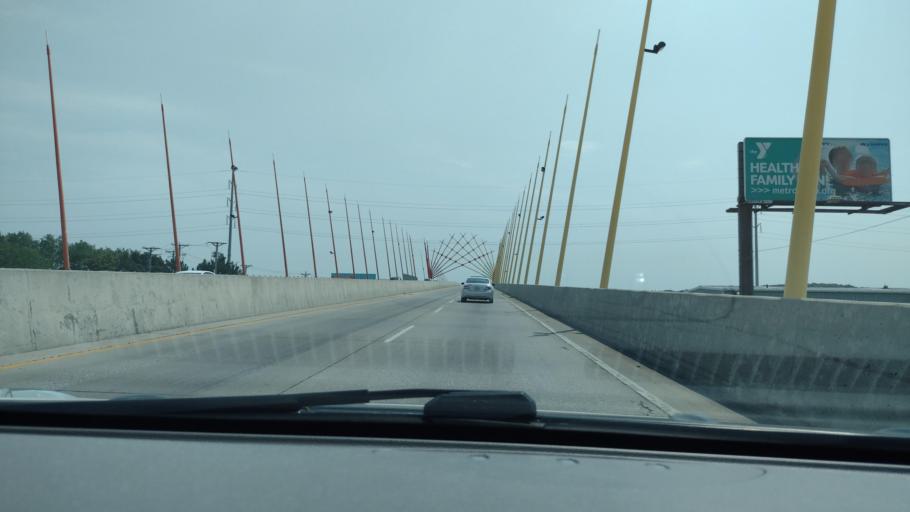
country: US
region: Iowa
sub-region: Pottawattamie County
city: Council Bluffs
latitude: 41.2619
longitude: -95.8648
